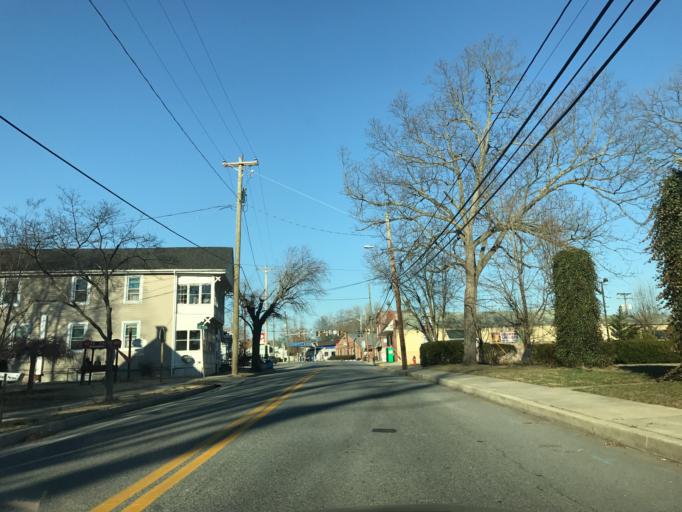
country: US
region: Delaware
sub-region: New Castle County
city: Townsend
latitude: 39.2576
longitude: -75.8381
